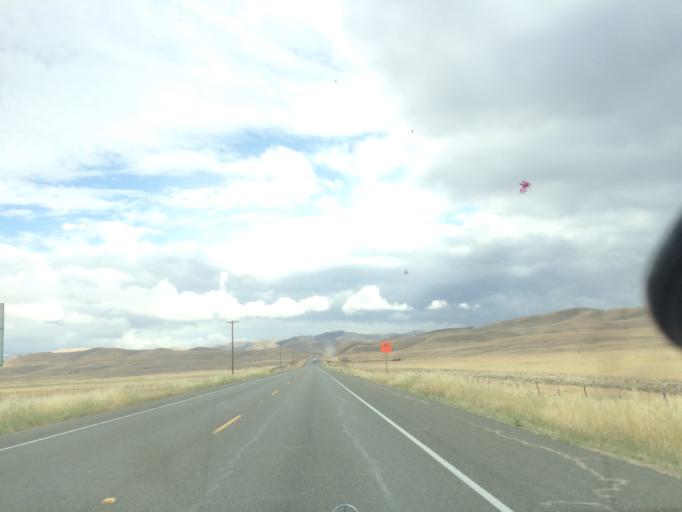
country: US
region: California
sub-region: San Luis Obispo County
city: Shandon
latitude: 35.7399
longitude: -120.2789
